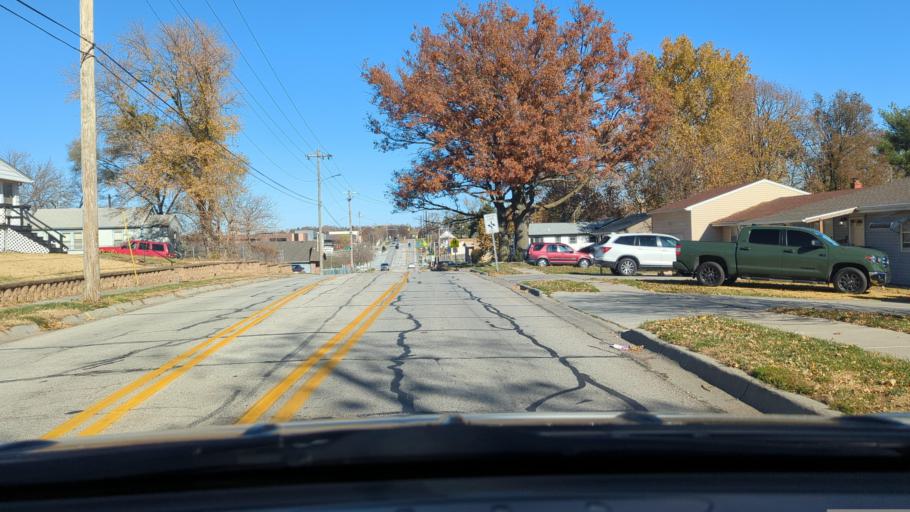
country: US
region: Nebraska
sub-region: Sarpy County
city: La Vista
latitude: 41.1970
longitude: -95.9770
